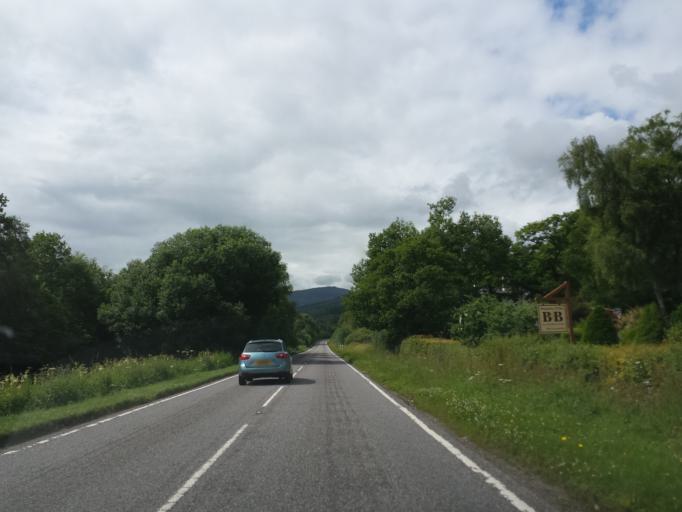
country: GB
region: Scotland
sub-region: Highland
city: Fort William
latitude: 56.8491
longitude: -5.1642
